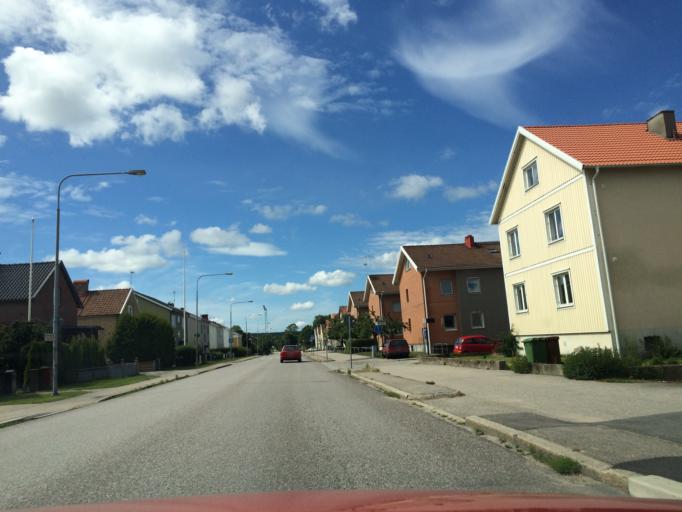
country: SE
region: Vaestra Goetaland
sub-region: Trollhattan
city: Trollhattan
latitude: 58.2887
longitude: 12.3202
